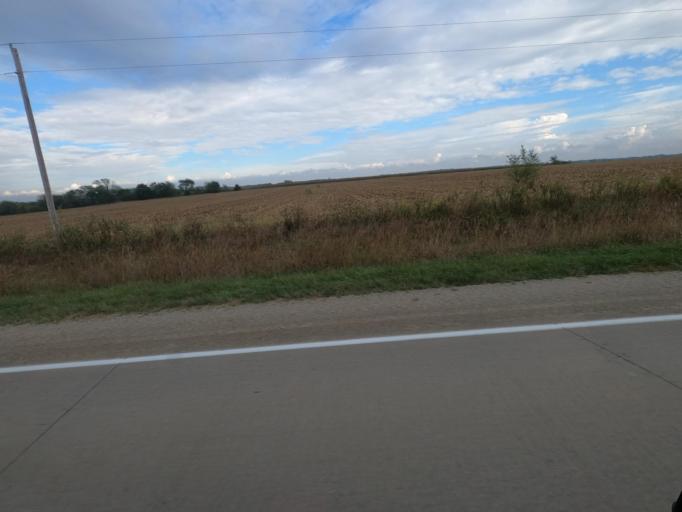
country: US
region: Iowa
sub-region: Henry County
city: Mount Pleasant
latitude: 40.8034
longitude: -91.7042
